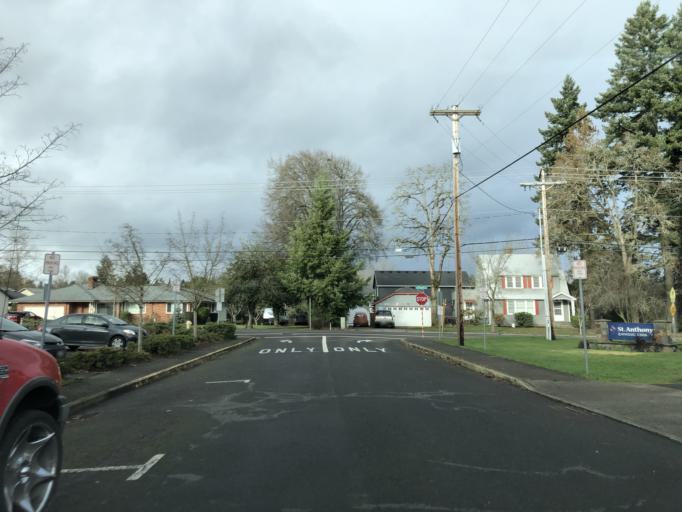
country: US
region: Oregon
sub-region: Washington County
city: Tigard
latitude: 45.4286
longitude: -122.7789
